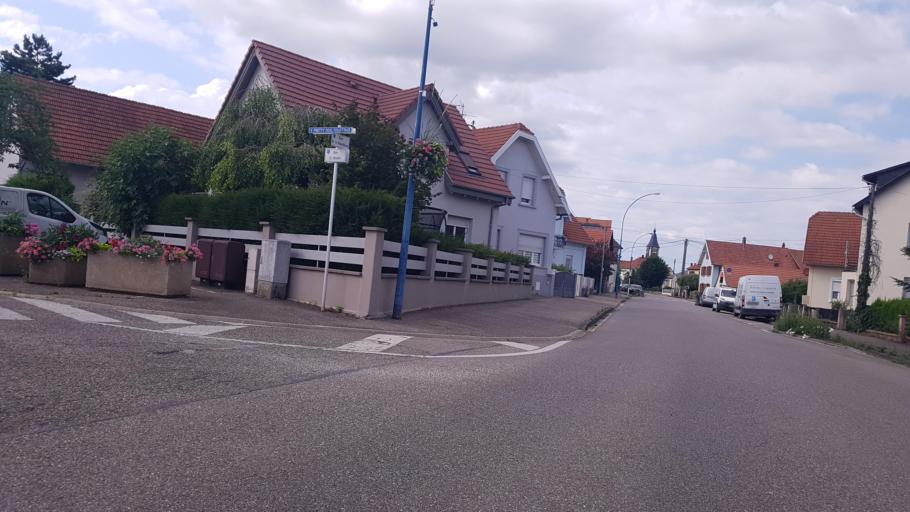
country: FR
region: Alsace
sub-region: Departement du Bas-Rhin
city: Weyersheim
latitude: 48.7136
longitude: 7.8016
